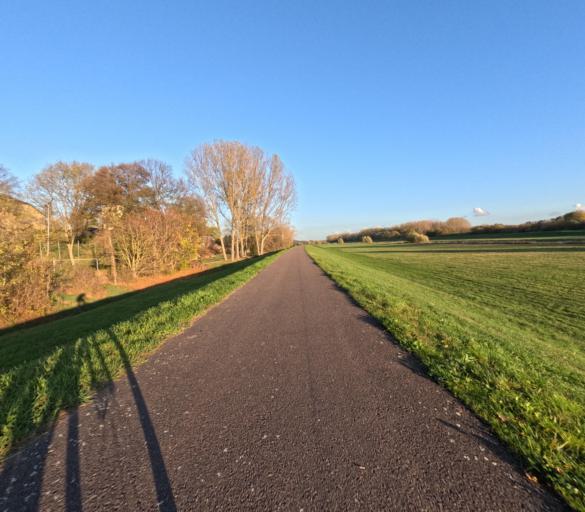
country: DE
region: Saxony-Anhalt
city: Rassnitz
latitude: 51.3918
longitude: 12.1068
